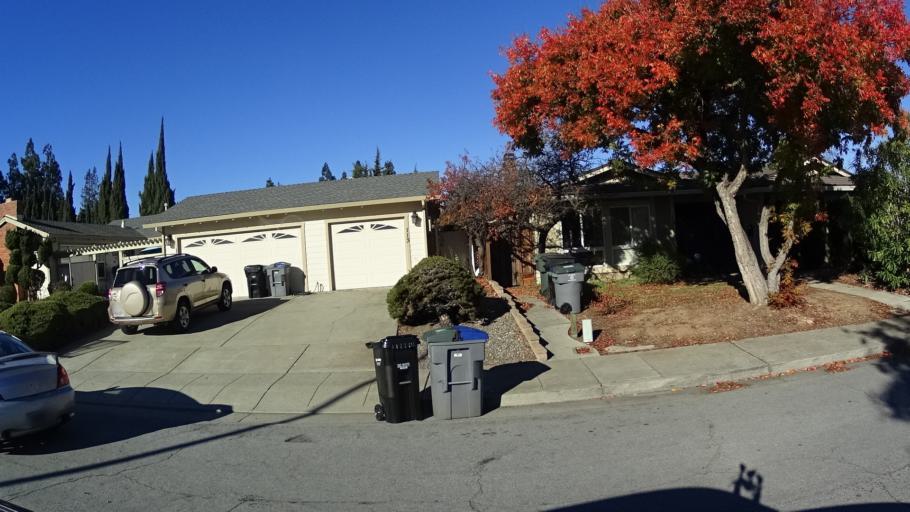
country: US
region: California
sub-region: Santa Clara County
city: Cupertino
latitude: 37.3407
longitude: -122.0316
